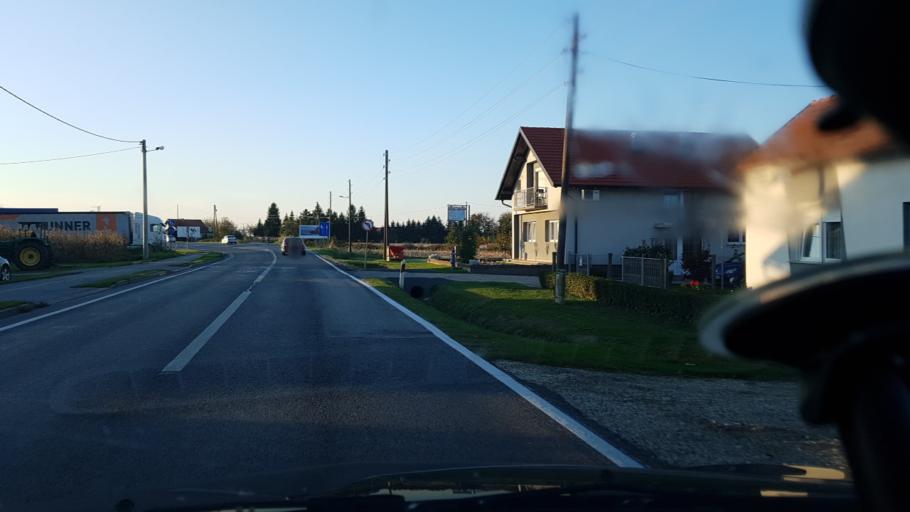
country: HR
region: Koprivnicko-Krizevacka
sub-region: Grad Koprivnica
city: Koprivnica
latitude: 46.1364
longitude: 16.8577
